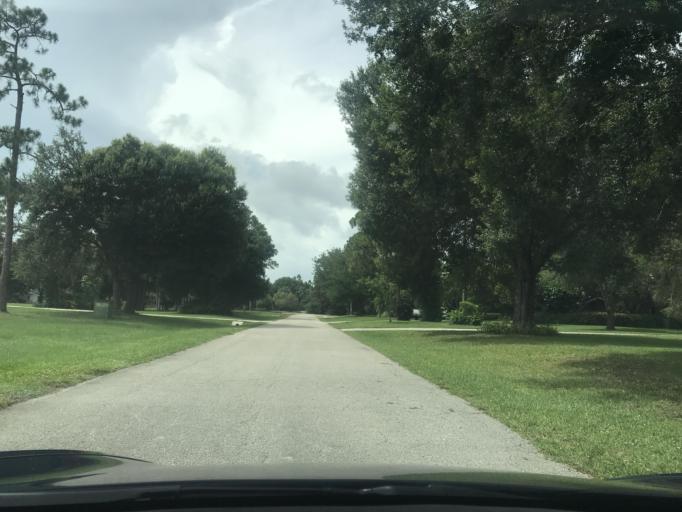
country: US
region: Florida
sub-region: Indian River County
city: West Vero Corridor
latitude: 27.6007
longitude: -80.5014
